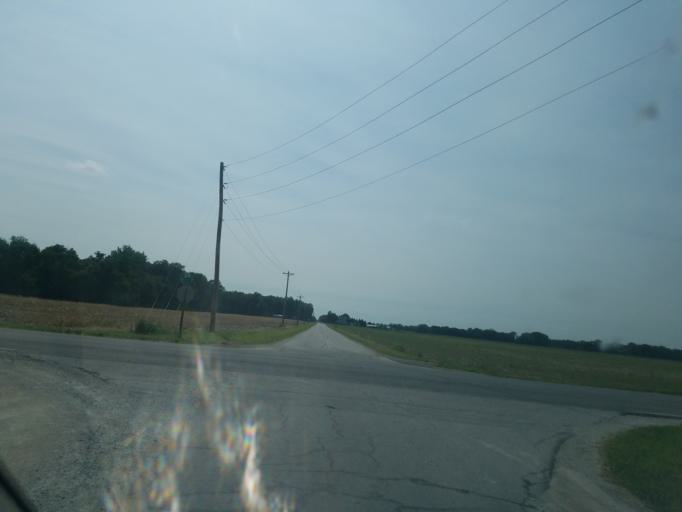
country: US
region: Ohio
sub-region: Seneca County
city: Tiffin
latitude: 41.1089
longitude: -83.2854
